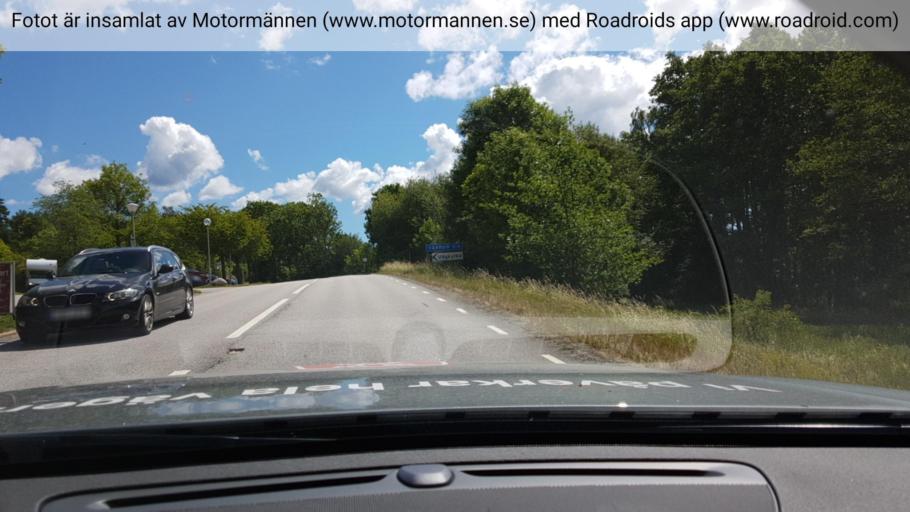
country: SE
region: Stockholm
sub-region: Varmdo Kommun
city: Hemmesta
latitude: 59.3574
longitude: 18.4961
